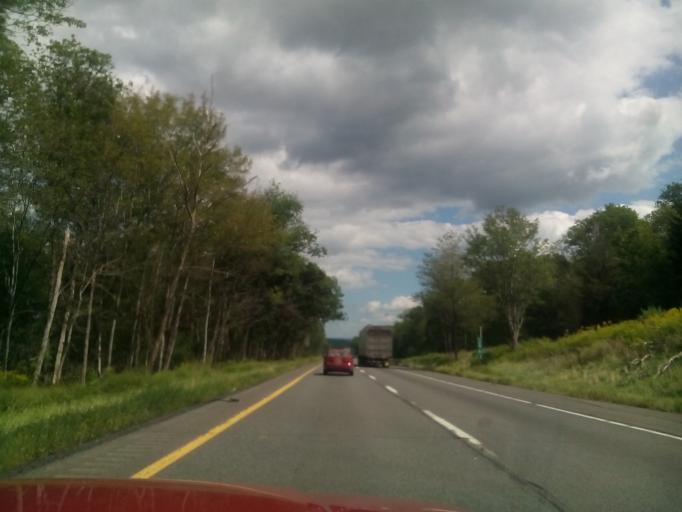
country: US
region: Pennsylvania
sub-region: Monroe County
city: Tannersville
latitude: 41.0634
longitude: -75.3444
